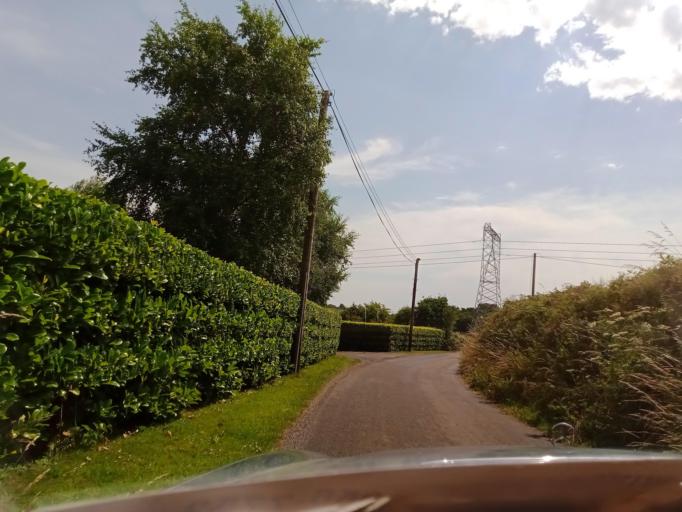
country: IE
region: Leinster
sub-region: Kilkenny
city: Mooncoin
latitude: 52.2678
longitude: -7.2118
